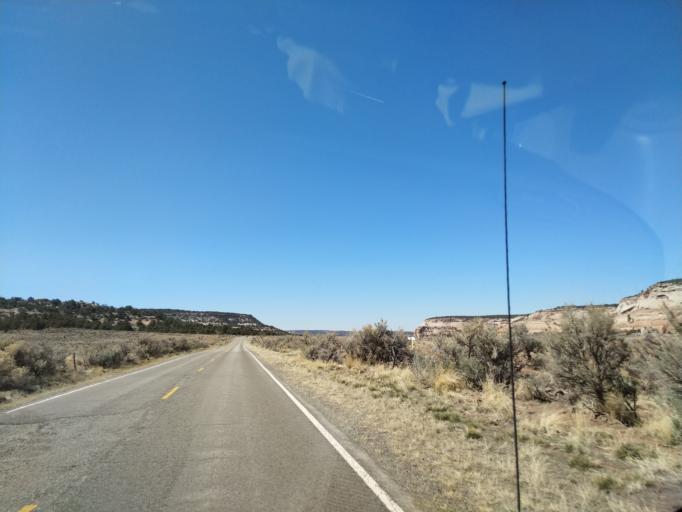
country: US
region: Colorado
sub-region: Mesa County
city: Loma
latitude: 38.9963
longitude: -108.8565
